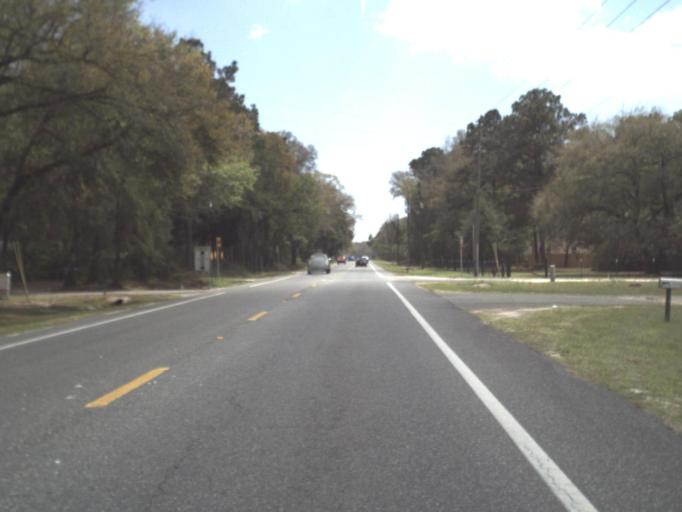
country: US
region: Florida
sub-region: Wakulla County
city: Crawfordville
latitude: 30.1162
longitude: -84.3832
